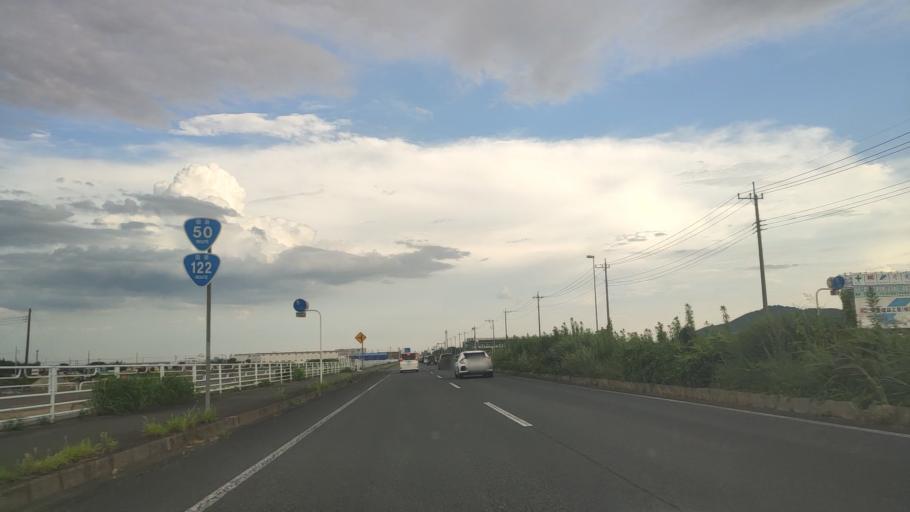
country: JP
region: Gunma
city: Ota
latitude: 36.3529
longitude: 139.3769
